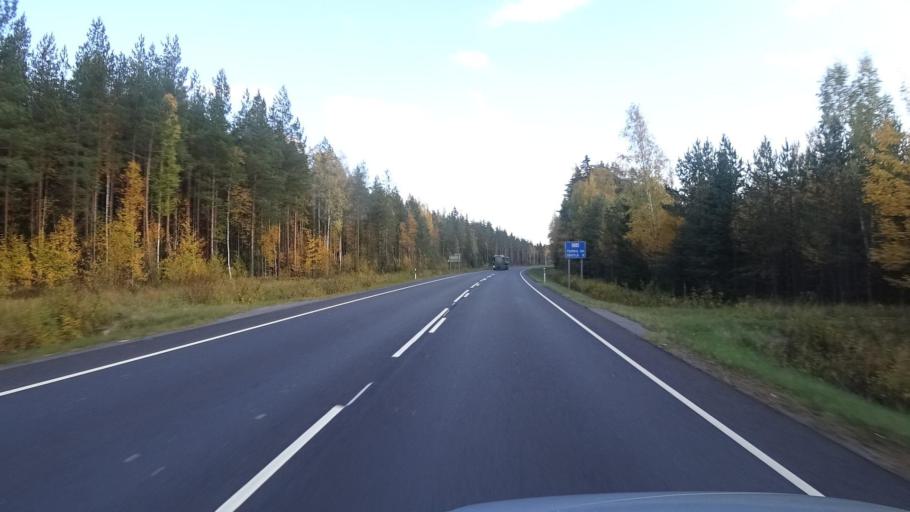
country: FI
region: Satakunta
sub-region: Rauma
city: Koeylioe
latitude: 61.1047
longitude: 22.2278
